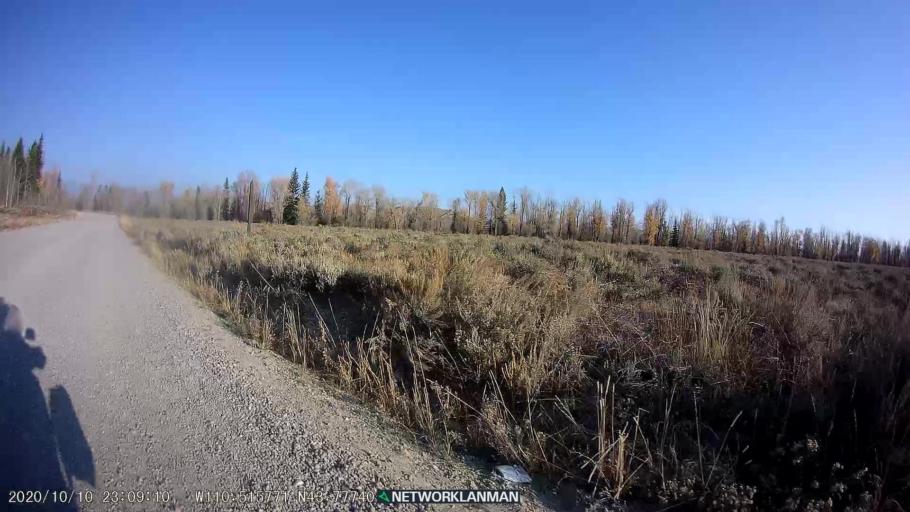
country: US
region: Wyoming
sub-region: Teton County
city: Jackson
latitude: 43.7776
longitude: -110.5173
